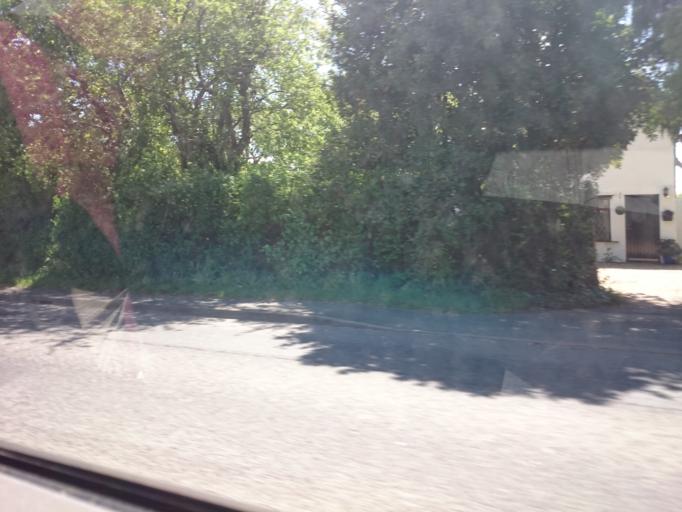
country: GB
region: England
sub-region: Hampshire
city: Totton
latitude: 50.9160
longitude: -1.5326
